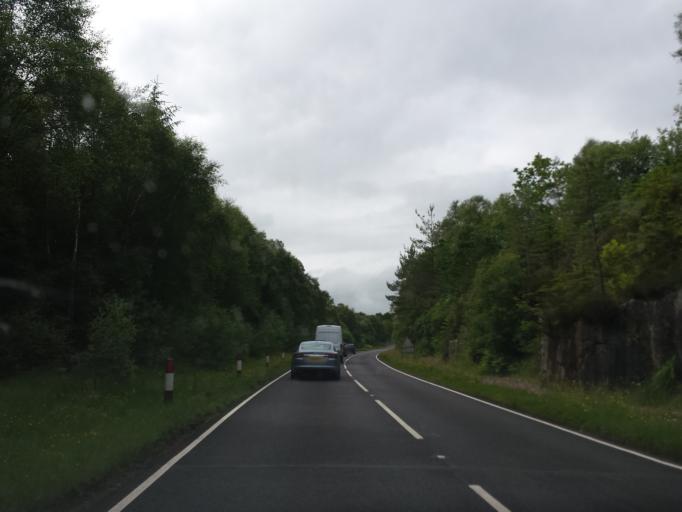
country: GB
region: Scotland
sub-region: Highland
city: Fort William
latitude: 56.8585
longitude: -5.3618
